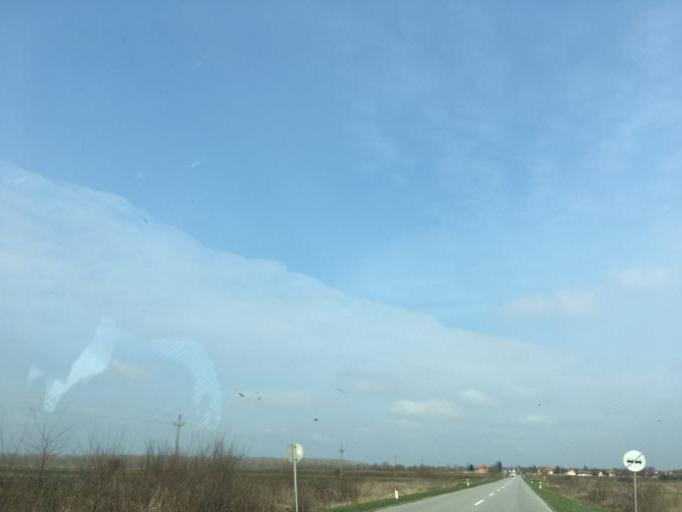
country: RS
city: Baranda
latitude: 45.0720
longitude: 20.4384
